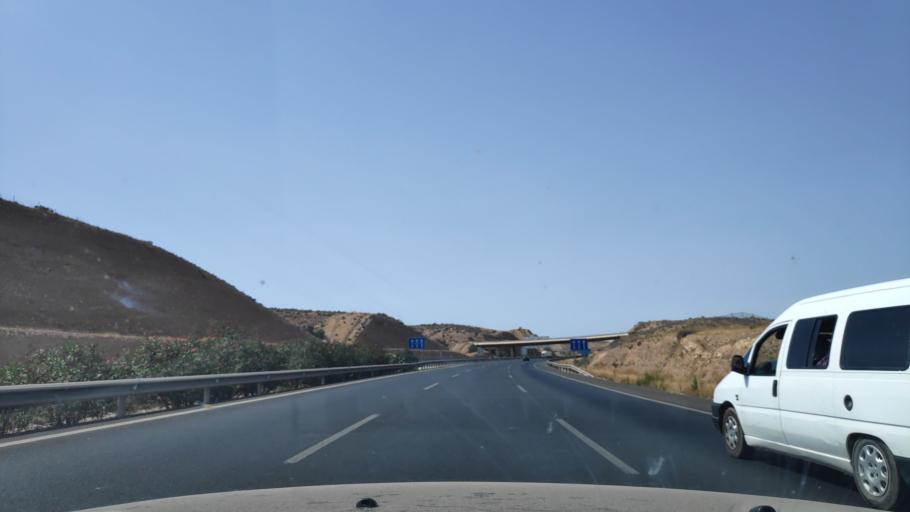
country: ES
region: Murcia
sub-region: Murcia
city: Molina de Segura
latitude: 38.0345
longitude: -1.1595
